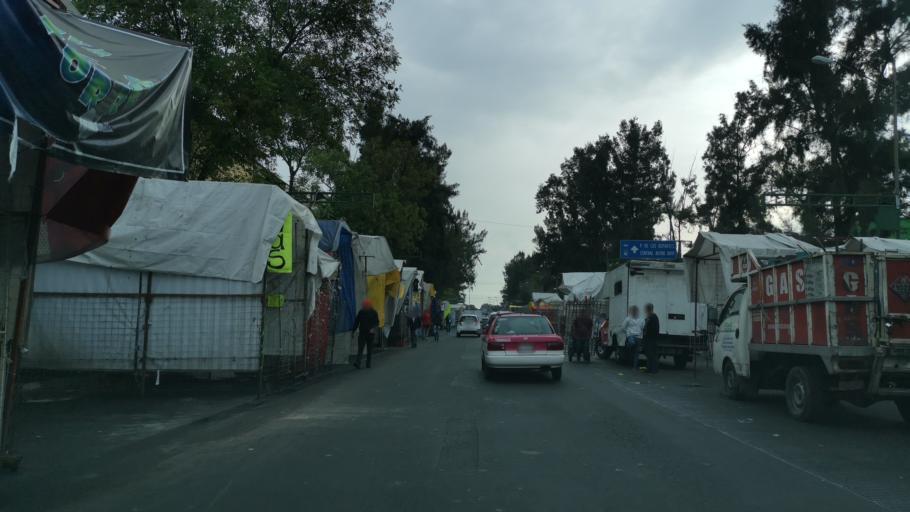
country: MX
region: Mexico City
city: Mexico City
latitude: 19.4431
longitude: -99.1272
